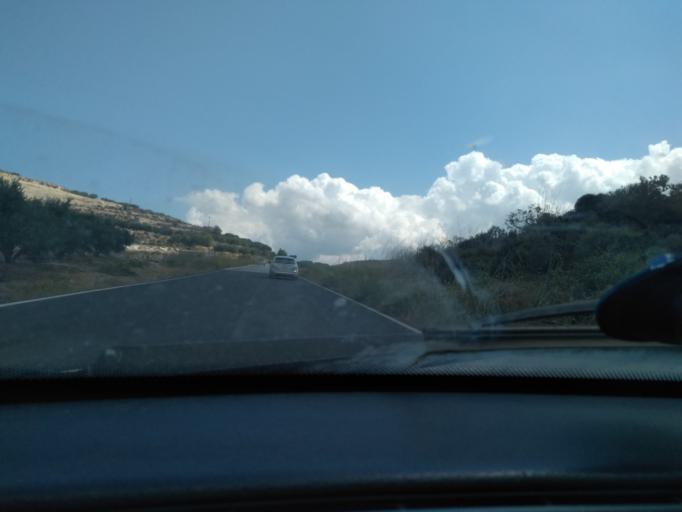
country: GR
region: Crete
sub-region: Nomos Lasithiou
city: Makry-Gialos
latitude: 35.0981
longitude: 26.0606
